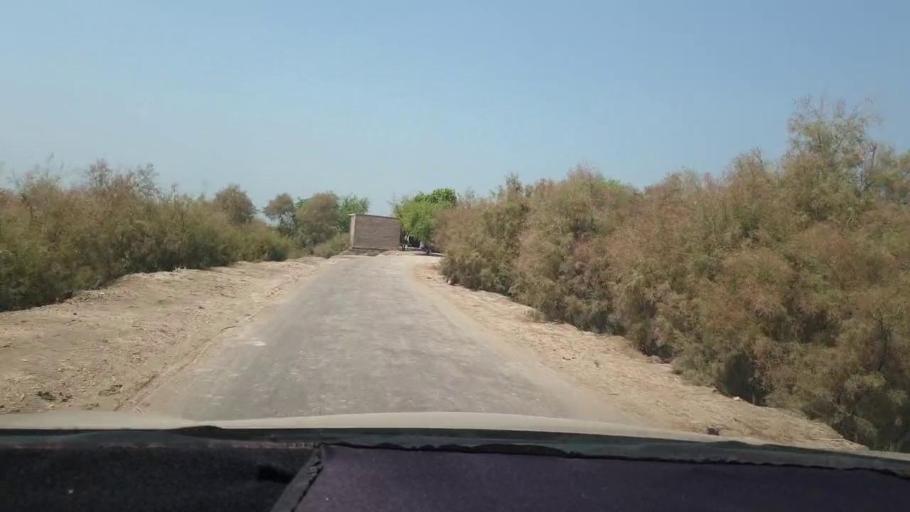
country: PK
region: Sindh
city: Miro Khan
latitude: 27.8620
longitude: 68.0817
